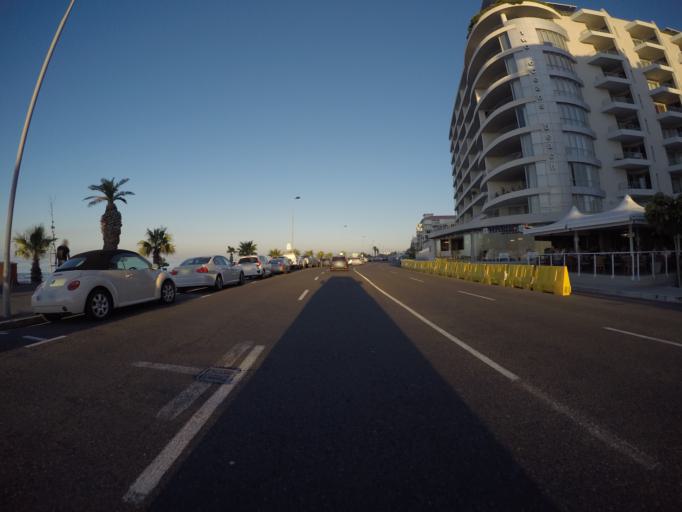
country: ZA
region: Western Cape
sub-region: City of Cape Town
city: Cape Town
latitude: -33.9000
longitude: 18.4054
